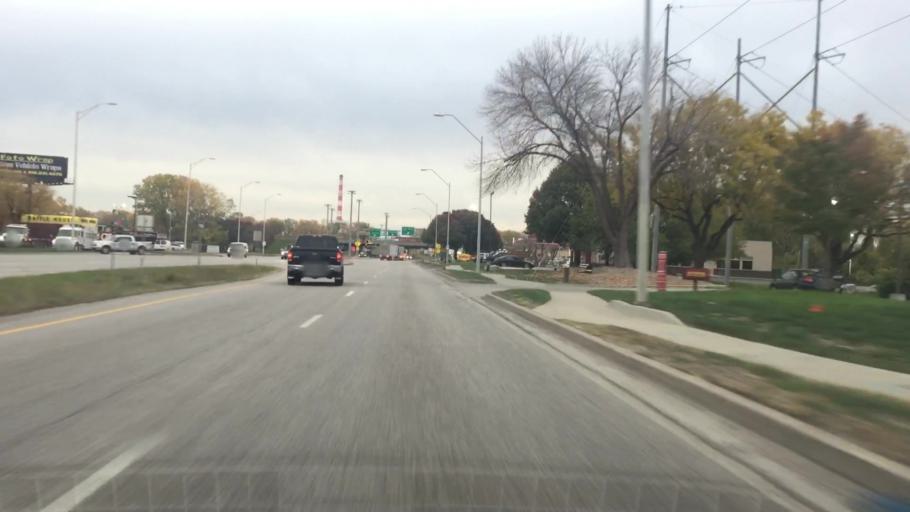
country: US
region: Missouri
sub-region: Clay County
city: North Kansas City
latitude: 39.1301
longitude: -94.5036
